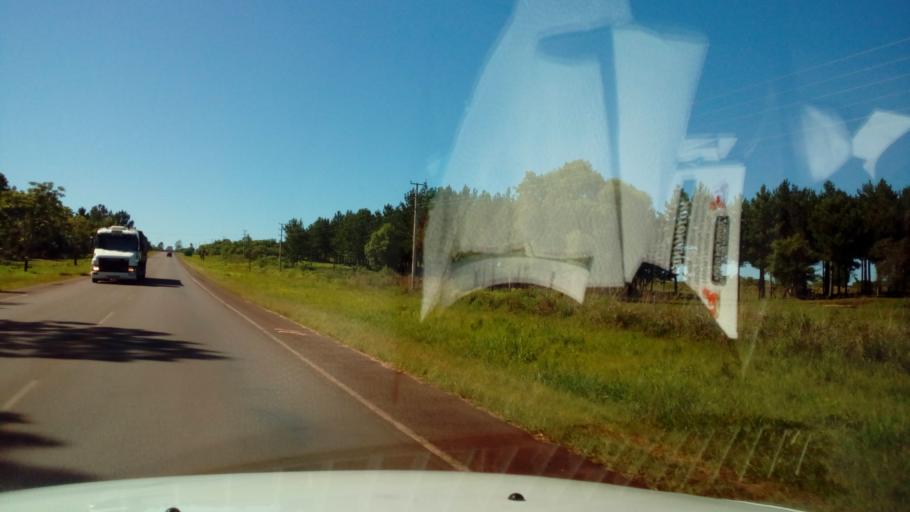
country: AR
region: Misiones
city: Santa Ana
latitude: -27.3996
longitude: -55.5589
